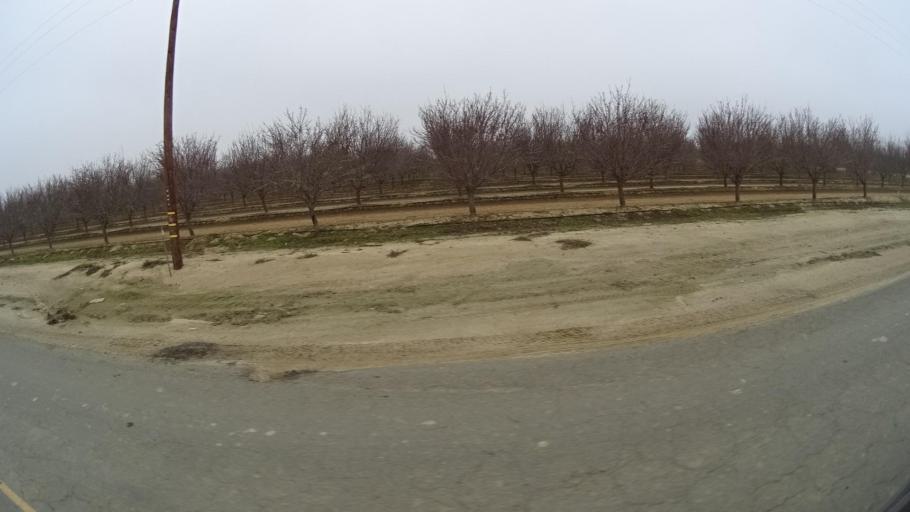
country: US
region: California
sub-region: Kern County
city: Lost Hills
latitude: 35.5949
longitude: -119.5269
